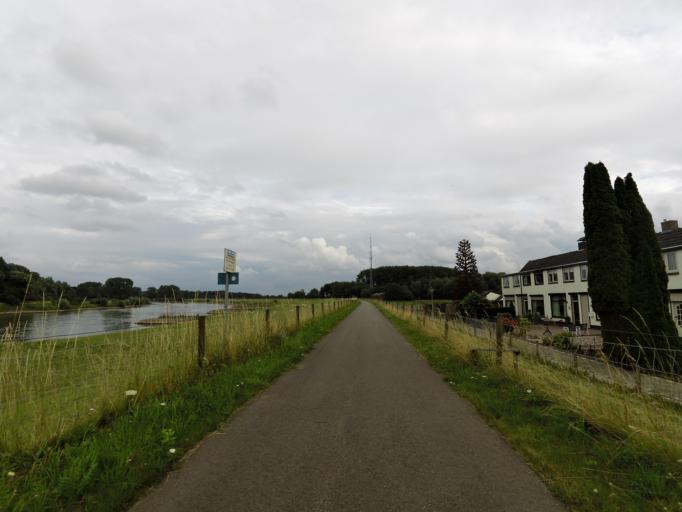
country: NL
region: Gelderland
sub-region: Gemeente Rheden
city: De Steeg
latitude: 51.9952
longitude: 6.0821
